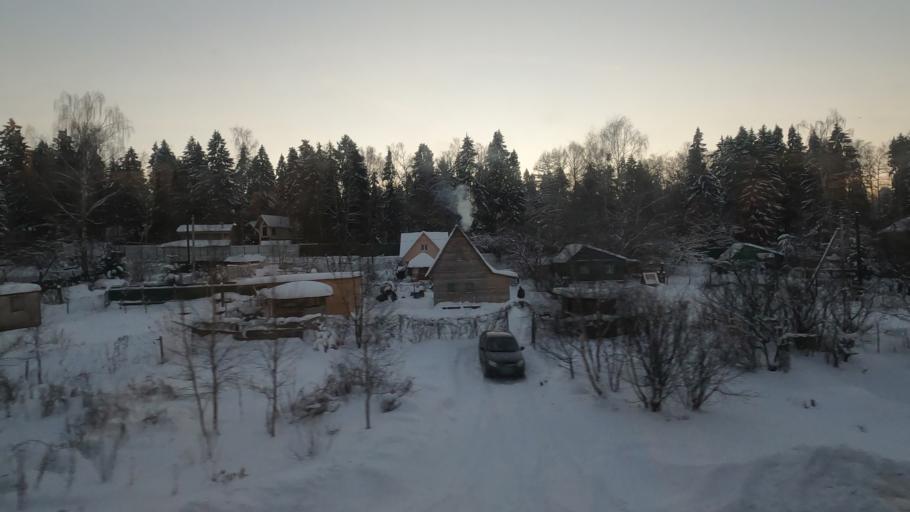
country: RU
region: Moskovskaya
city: Yermolino
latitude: 56.1378
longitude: 37.5091
